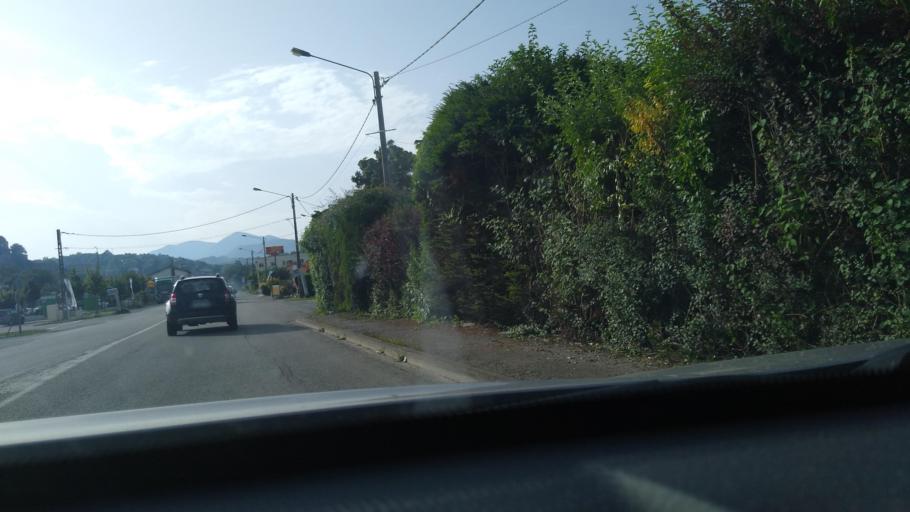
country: FR
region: Midi-Pyrenees
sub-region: Departement de l'Ariege
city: Saint-Lizier
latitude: 43.0049
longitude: 1.1272
